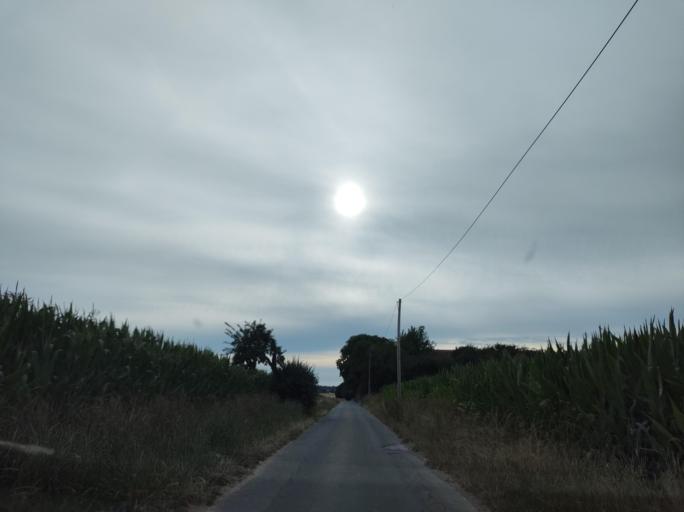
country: DE
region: North Rhine-Westphalia
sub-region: Regierungsbezirk Detmold
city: Salzkotten
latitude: 51.6512
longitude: 8.6340
